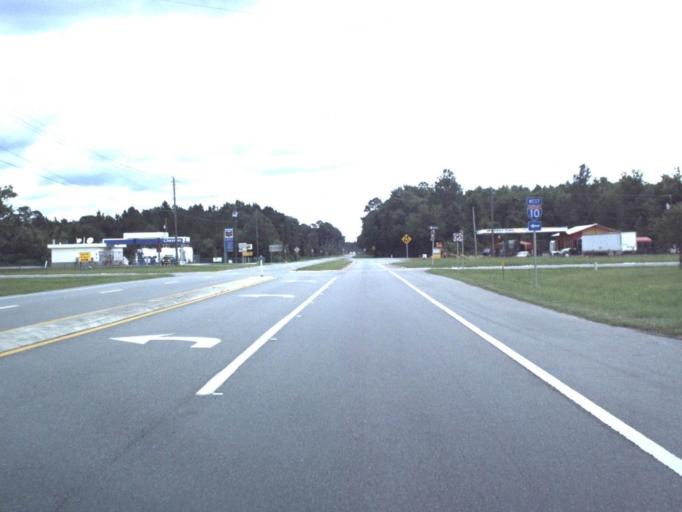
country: US
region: Florida
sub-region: Columbia County
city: Five Points
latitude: 30.2419
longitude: -82.6384
